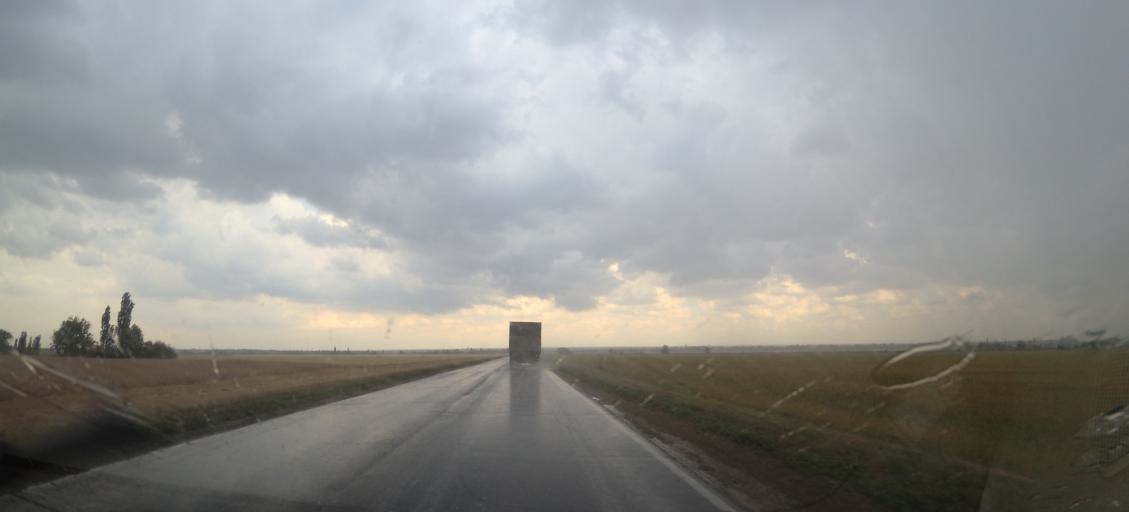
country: RU
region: Rostov
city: Orlovskiy
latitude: 46.8658
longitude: 41.9643
